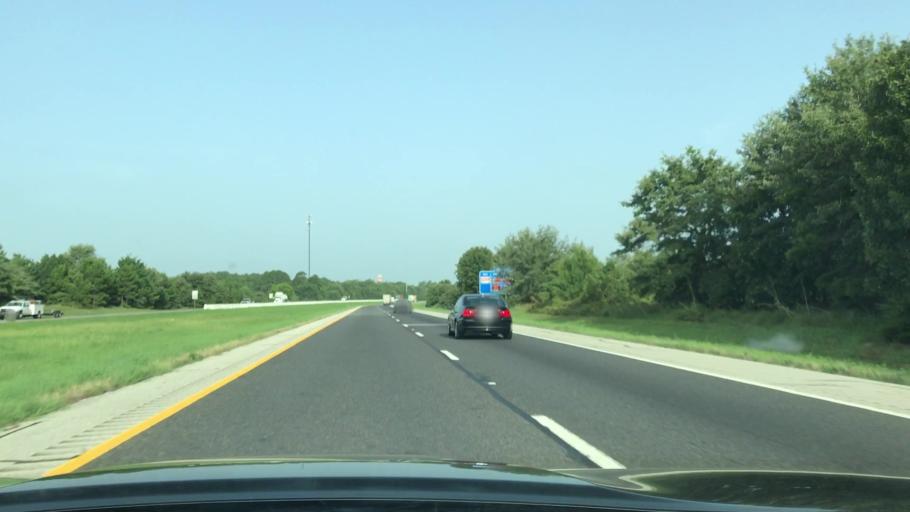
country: US
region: Texas
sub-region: Smith County
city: Tyler
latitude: 32.4522
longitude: -95.2705
